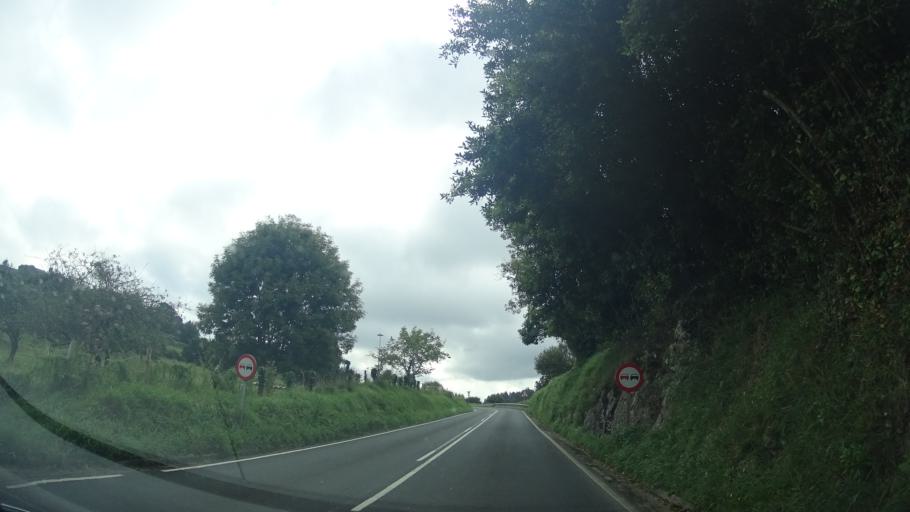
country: ES
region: Asturias
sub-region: Province of Asturias
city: Ribadesella
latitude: 43.4652
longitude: -5.1220
